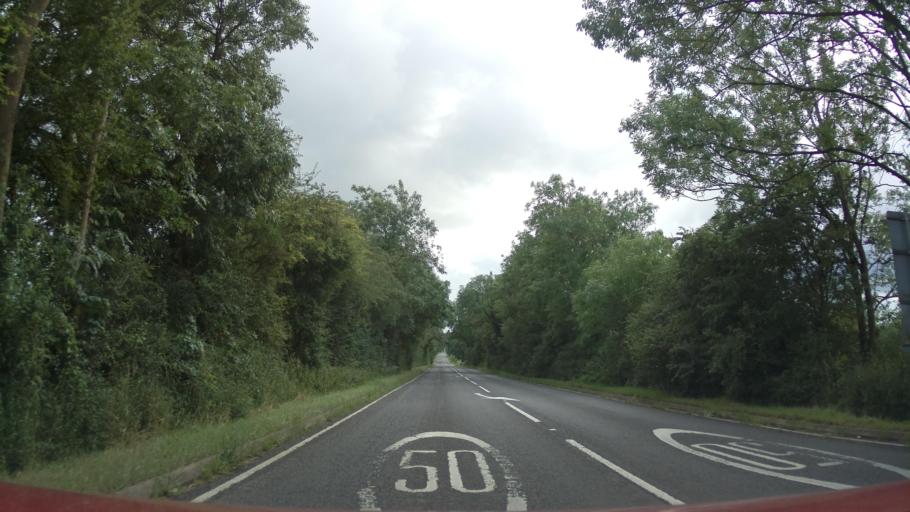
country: GB
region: England
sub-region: Warwickshire
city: Long Itchington
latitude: 52.2915
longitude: -1.3482
